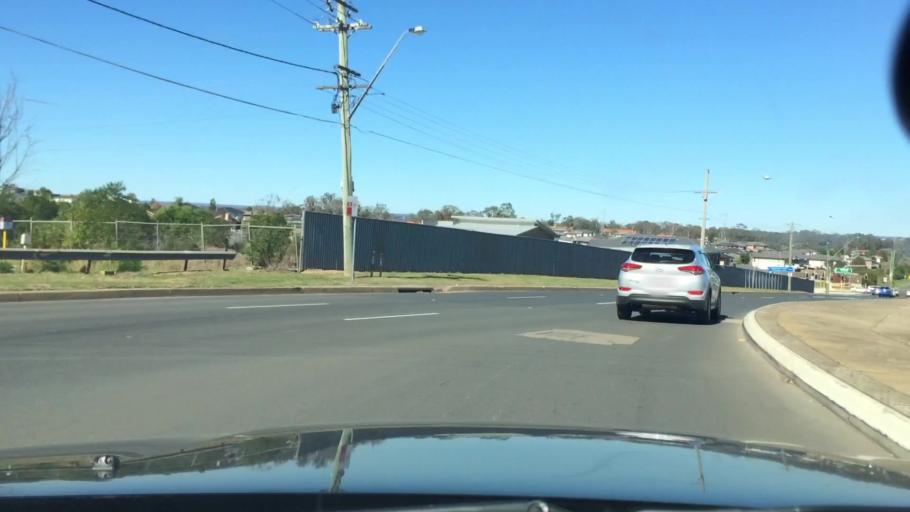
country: AU
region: New South Wales
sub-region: Campbelltown Municipality
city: Glenfield
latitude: -33.9581
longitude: 150.8871
